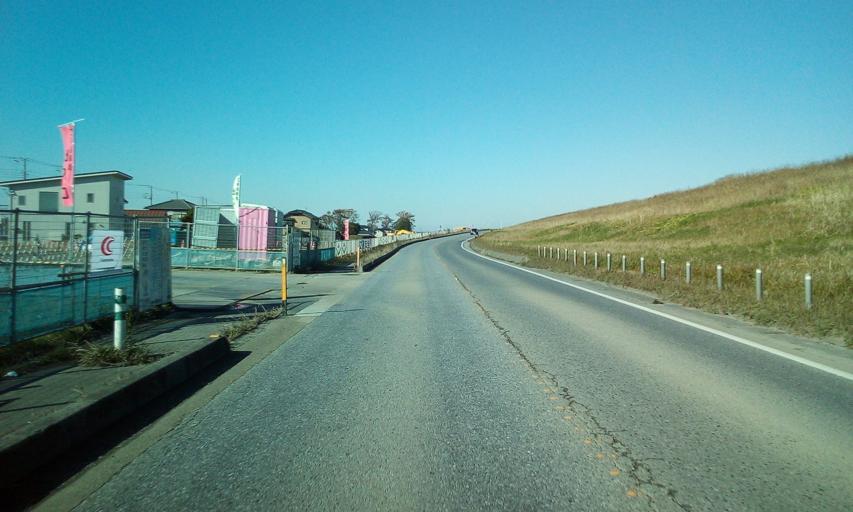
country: JP
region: Chiba
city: Noda
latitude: 35.9333
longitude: 139.8507
